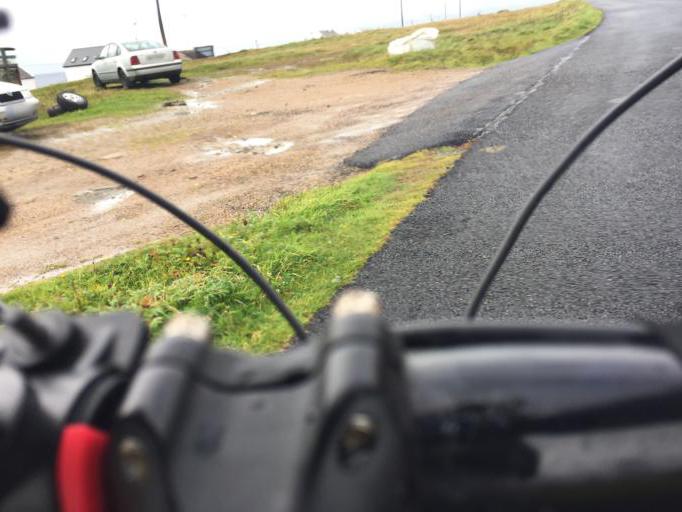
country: IE
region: Ulster
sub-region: County Donegal
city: Derrybeg
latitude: 55.2586
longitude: -8.2077
